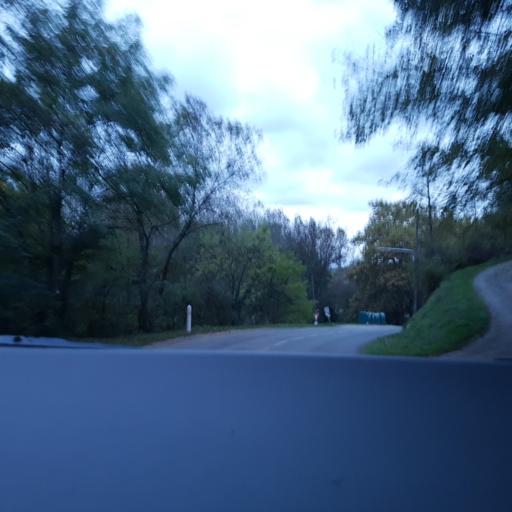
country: FR
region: Midi-Pyrenees
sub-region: Departement du Gers
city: Montreal
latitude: 43.9489
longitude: 0.1981
